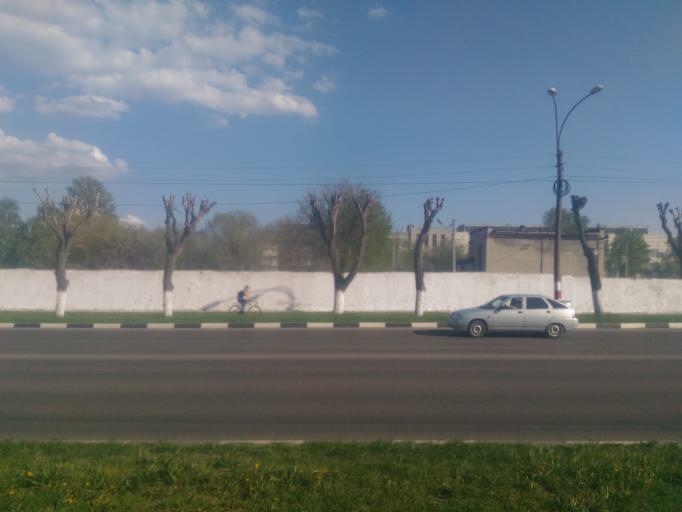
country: RU
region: Ulyanovsk
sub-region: Ulyanovskiy Rayon
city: Ulyanovsk
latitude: 54.2870
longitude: 48.3609
